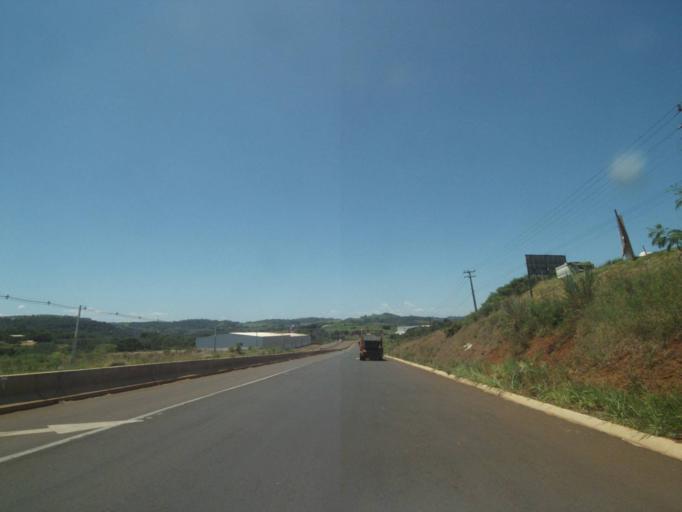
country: BR
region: Parana
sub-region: Londrina
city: Londrina
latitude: -23.3919
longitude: -51.1341
